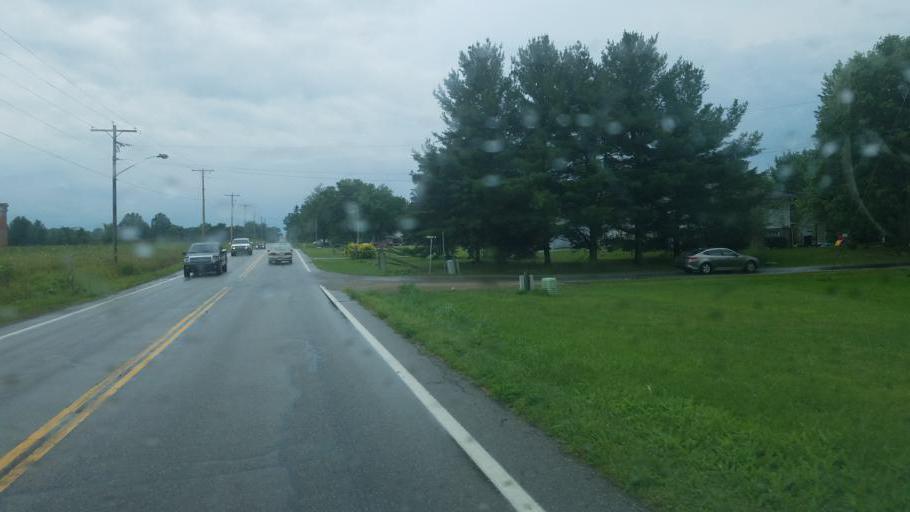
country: US
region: Ohio
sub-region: Ashtabula County
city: Orwell
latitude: 41.4348
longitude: -80.8688
